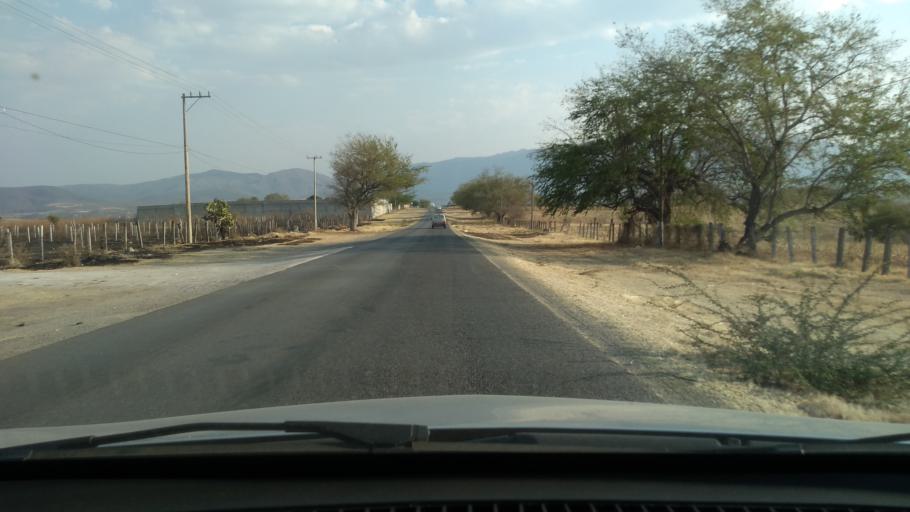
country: MX
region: Morelos
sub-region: Jojutla
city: Tehuixtla
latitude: 18.5818
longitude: -99.2641
